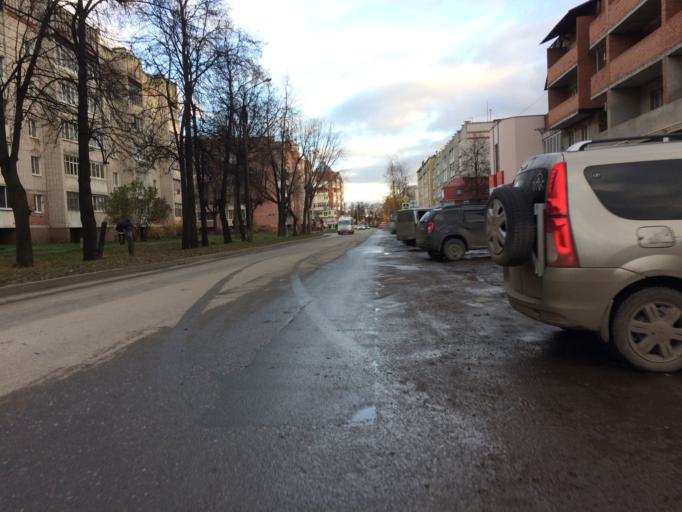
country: RU
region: Mariy-El
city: Yoshkar-Ola
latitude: 56.6442
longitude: 47.8997
